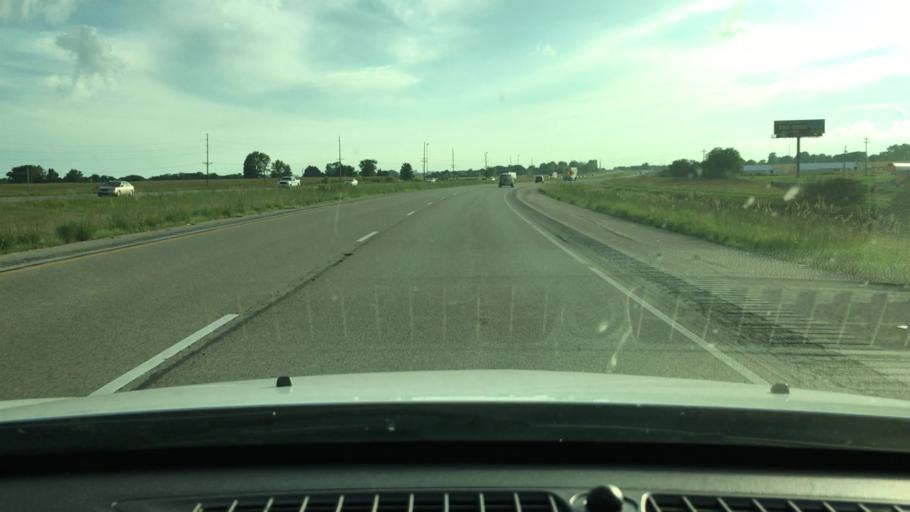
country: US
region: Illinois
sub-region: Logan County
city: Atlanta
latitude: 40.3106
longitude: -89.1646
